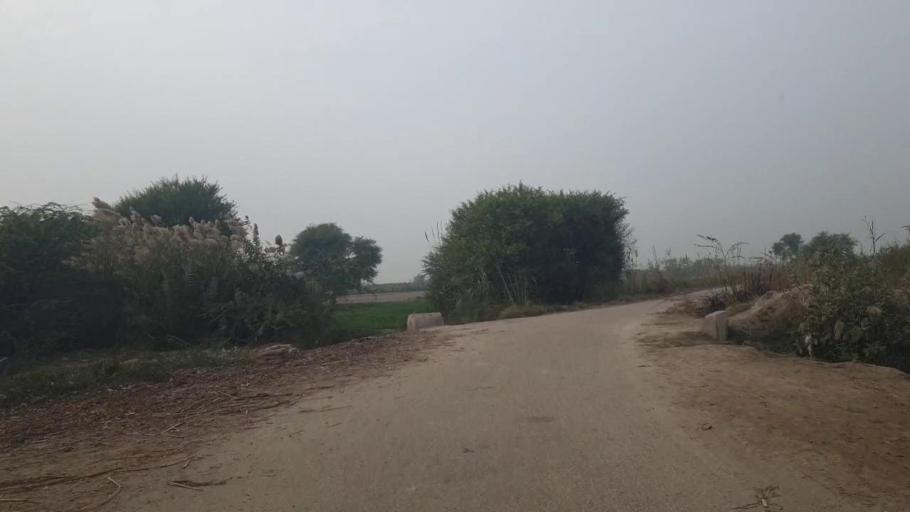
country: PK
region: Sindh
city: Tando Adam
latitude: 25.8156
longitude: 68.7154
